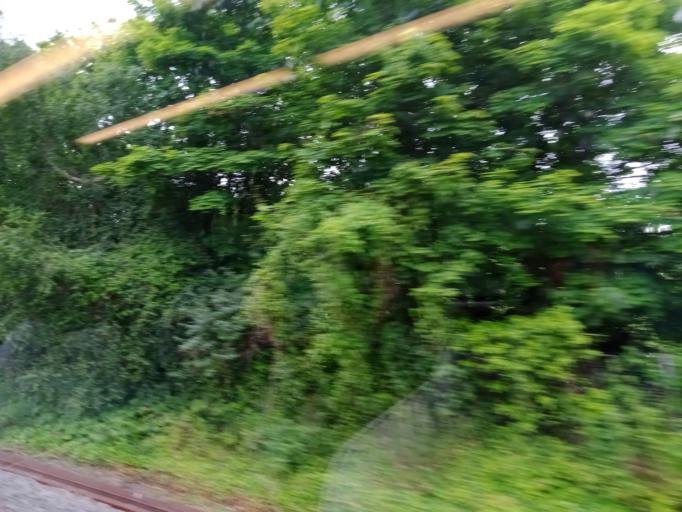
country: GB
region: Wales
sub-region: Conwy
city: Conwy
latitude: 53.2796
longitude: -3.8285
